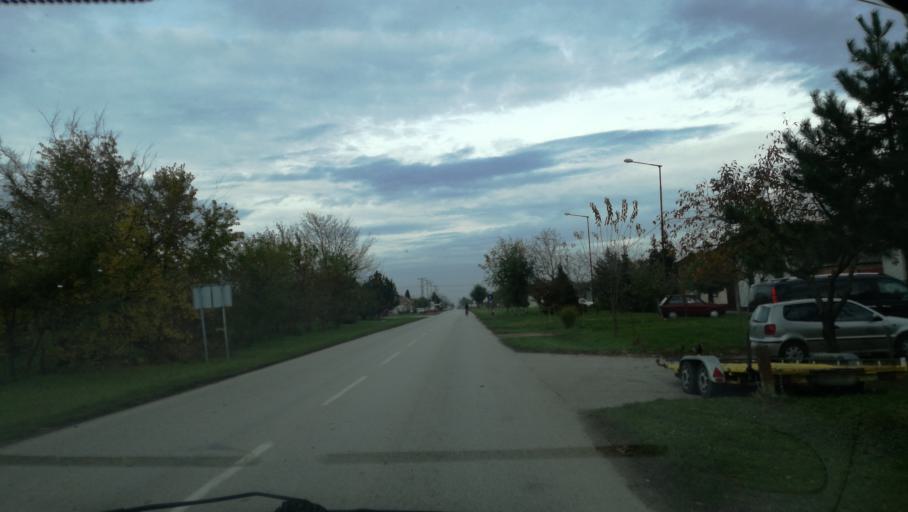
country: RS
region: Autonomna Pokrajina Vojvodina
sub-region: Severnobanatski Okrug
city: Kikinda
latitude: 45.8386
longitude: 20.4542
